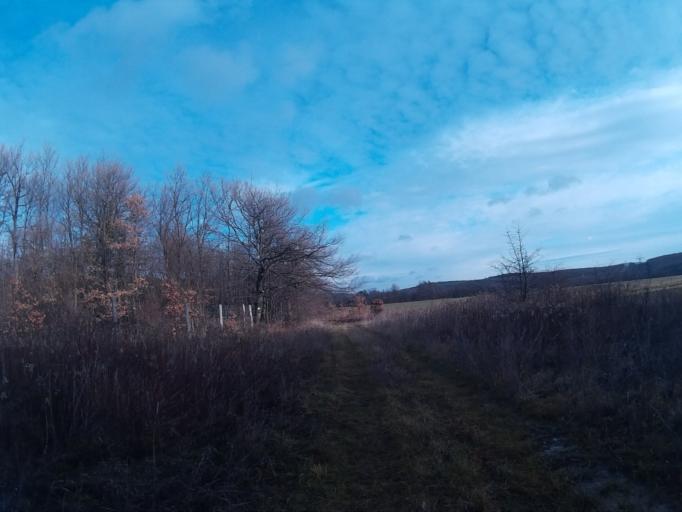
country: HU
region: Veszprem
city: Urkut
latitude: 47.0903
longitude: 17.6574
